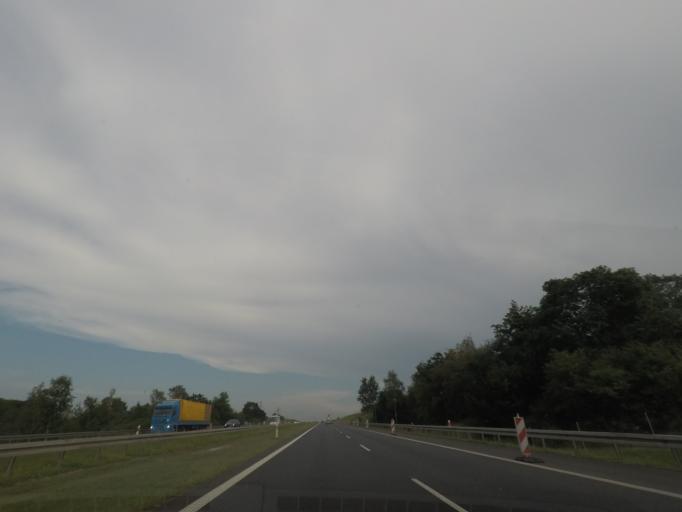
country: PL
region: Silesian Voivodeship
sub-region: Powiat bierunsko-ledzinski
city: Imielin
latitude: 50.1778
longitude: 19.2014
